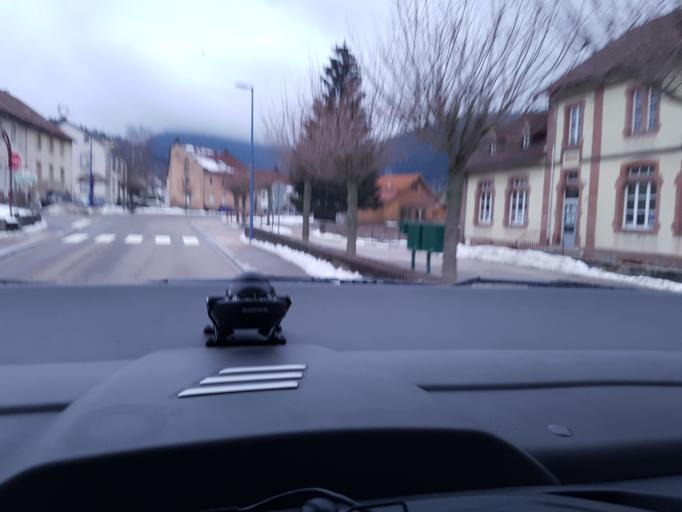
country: FR
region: Lorraine
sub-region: Departement des Vosges
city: Plainfaing
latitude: 48.1589
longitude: 7.0092
